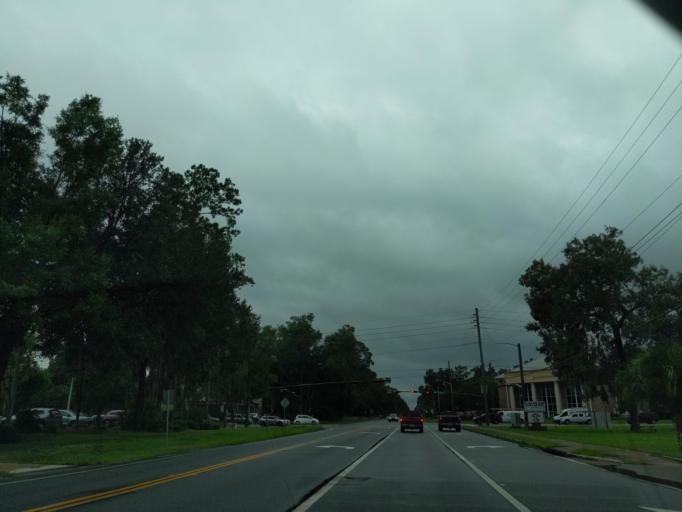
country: US
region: Florida
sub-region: Alachua County
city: Gainesville
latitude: 29.6314
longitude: -82.4225
